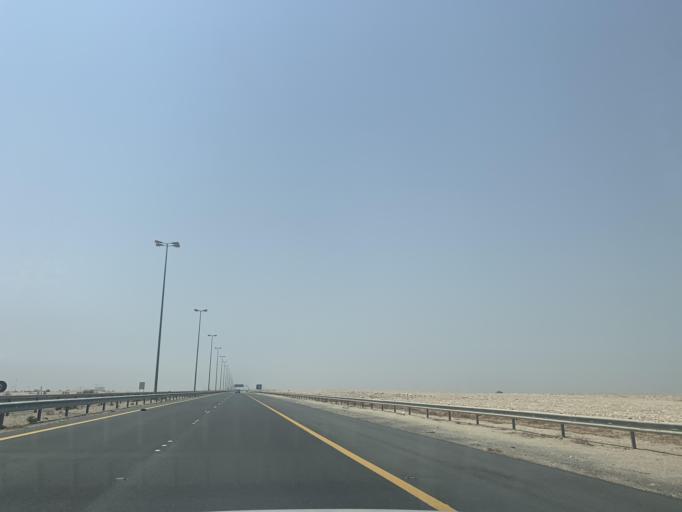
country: BH
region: Central Governorate
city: Dar Kulayb
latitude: 25.8991
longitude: 50.5771
